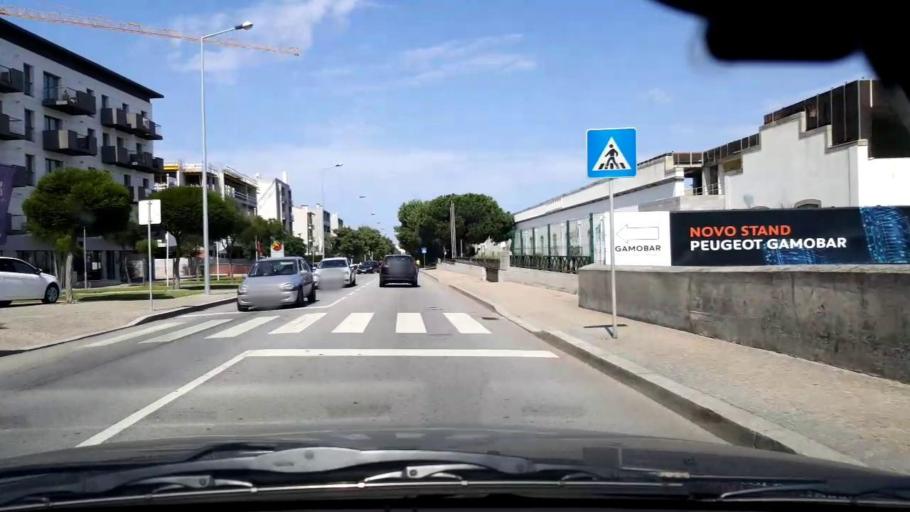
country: PT
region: Porto
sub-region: Povoa de Varzim
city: Povoa de Varzim
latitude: 41.3701
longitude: -8.7526
